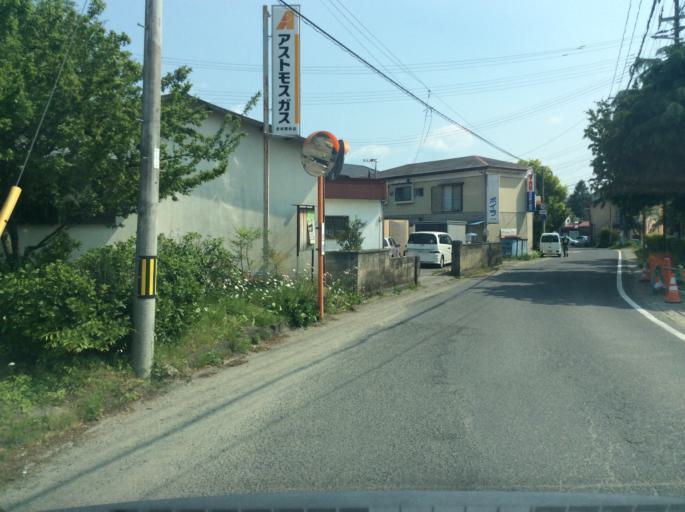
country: JP
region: Fukushima
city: Sukagawa
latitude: 37.1277
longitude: 140.2229
